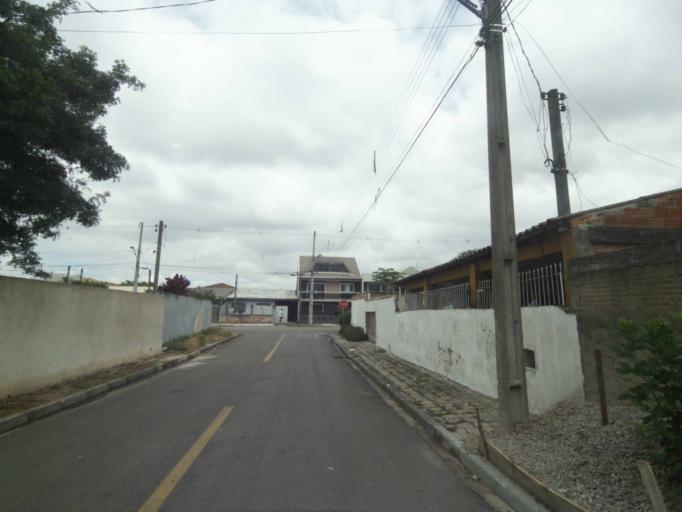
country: BR
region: Parana
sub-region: Pinhais
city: Pinhais
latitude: -25.4612
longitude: -49.1955
